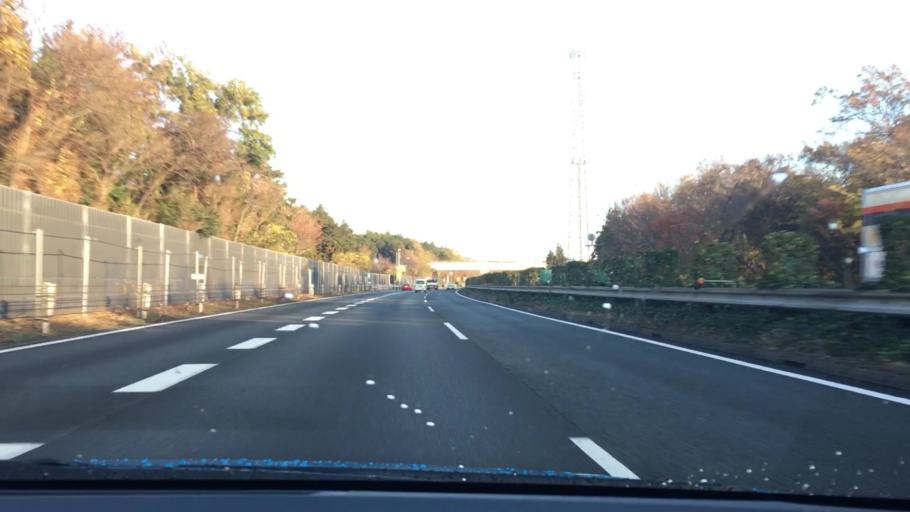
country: JP
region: Shizuoka
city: Gotemba
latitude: 35.2350
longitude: 138.9089
